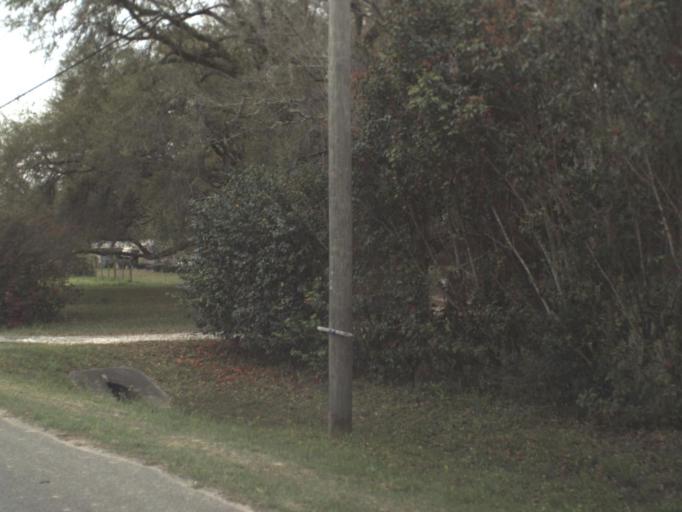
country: US
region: Florida
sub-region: Gulf County
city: Wewahitchka
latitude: 30.1252
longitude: -85.2016
